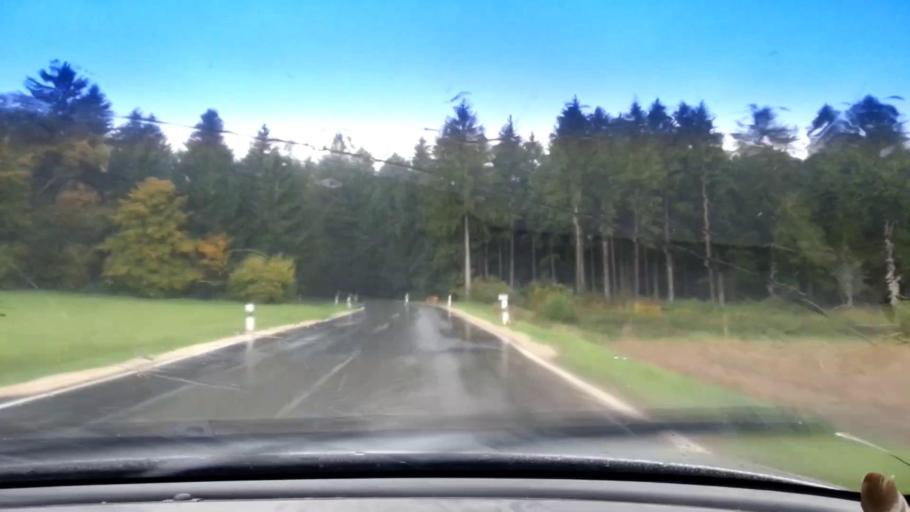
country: DE
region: Bavaria
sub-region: Upper Franconia
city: Wattendorf
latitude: 50.0401
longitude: 11.1297
